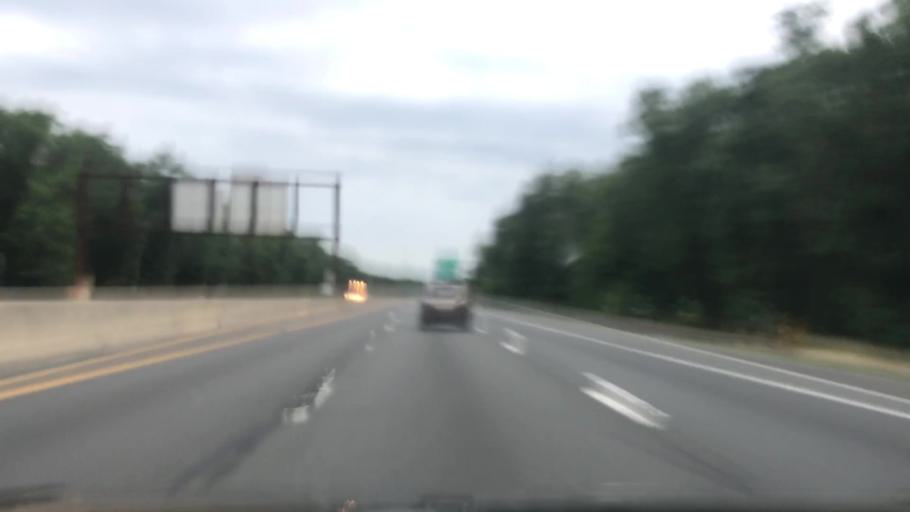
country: US
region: New Jersey
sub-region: Ocean County
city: Silver Ridge
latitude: 39.9761
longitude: -74.2113
